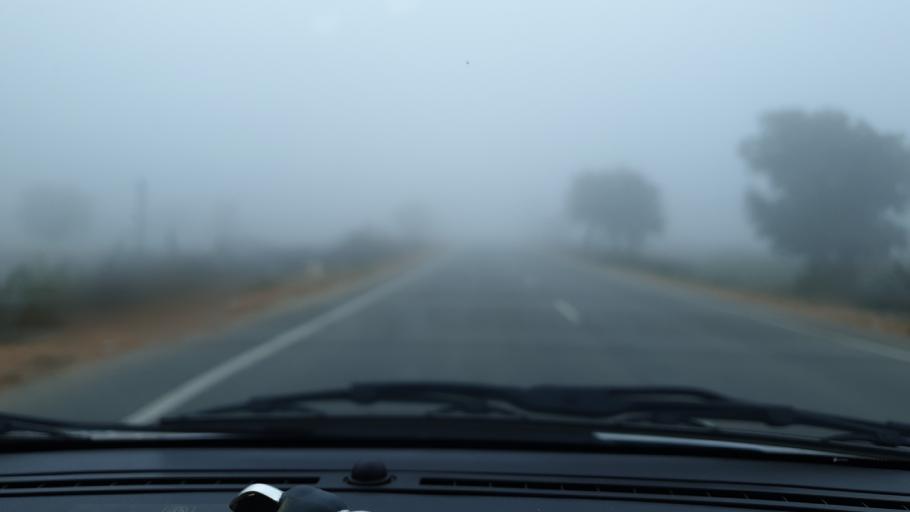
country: IN
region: Telangana
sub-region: Mahbubnagar
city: Nagar Karnul
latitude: 16.6865
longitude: 78.5231
